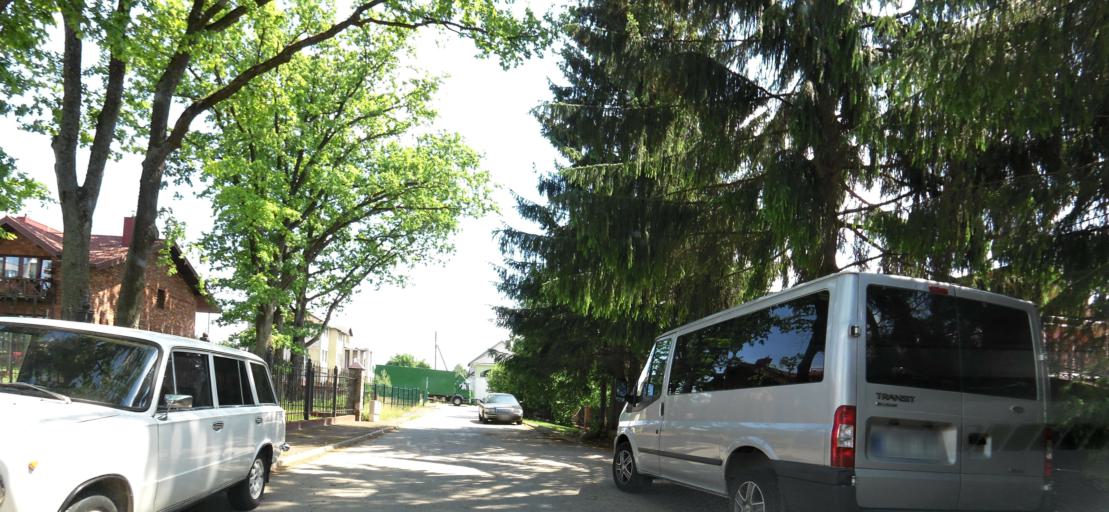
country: LT
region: Vilnius County
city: Pasilaiciai
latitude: 54.7606
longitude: 25.2073
